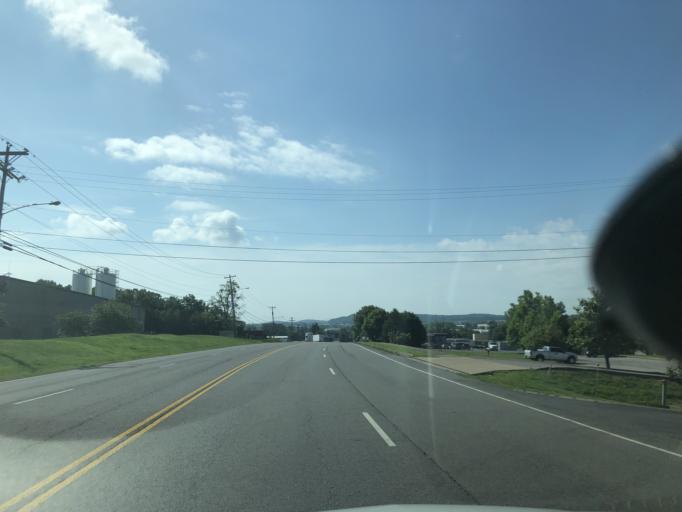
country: US
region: Tennessee
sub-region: Rutherford County
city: La Vergne
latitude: 36.0149
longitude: -86.6131
